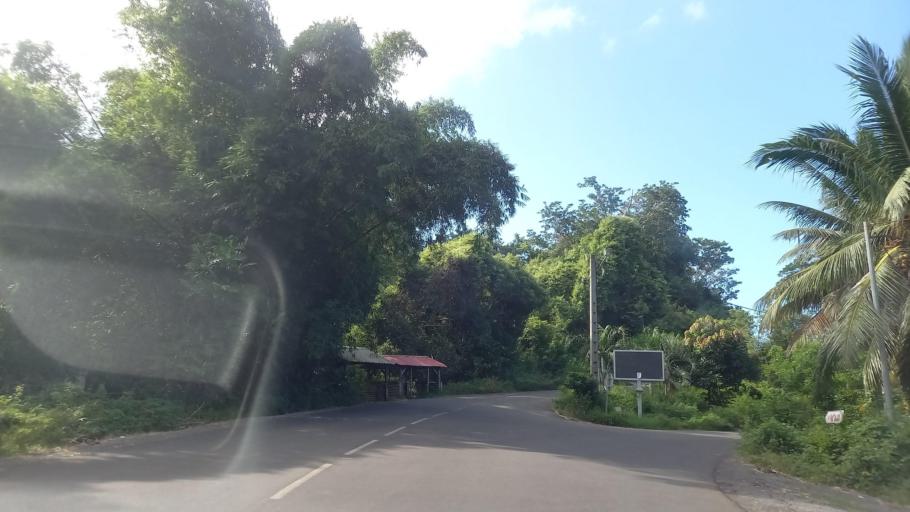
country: YT
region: Kani-Keli
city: Kani Keli
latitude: -12.9856
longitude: 45.1363
